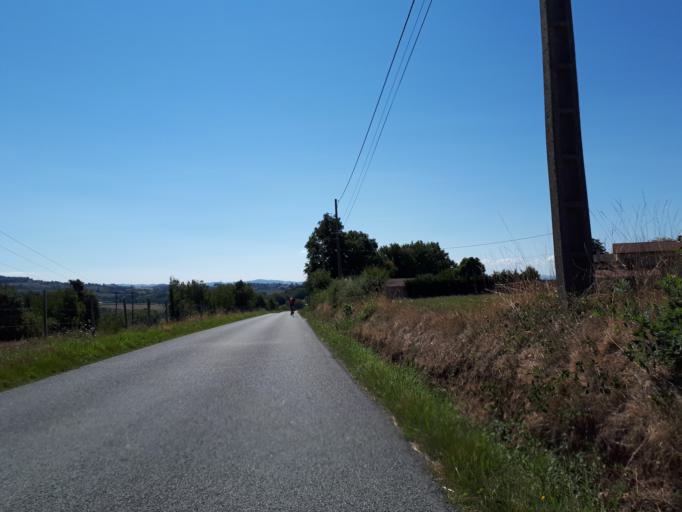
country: FR
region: Rhone-Alpes
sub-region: Departement de la Loire
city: Bussieres
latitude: 45.8218
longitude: 4.3033
